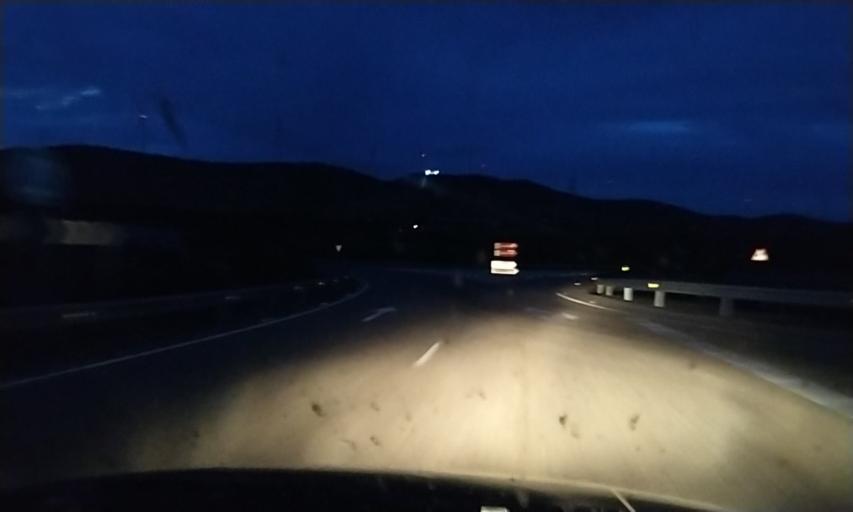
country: ES
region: Extremadura
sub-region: Provincia de Caceres
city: Plasencia
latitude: 39.9811
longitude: -6.1515
